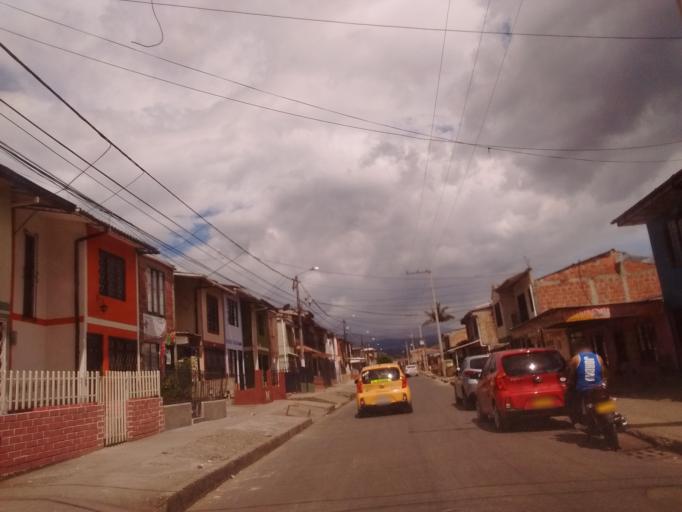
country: CO
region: Cauca
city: Popayan
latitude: 2.4768
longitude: -76.5614
